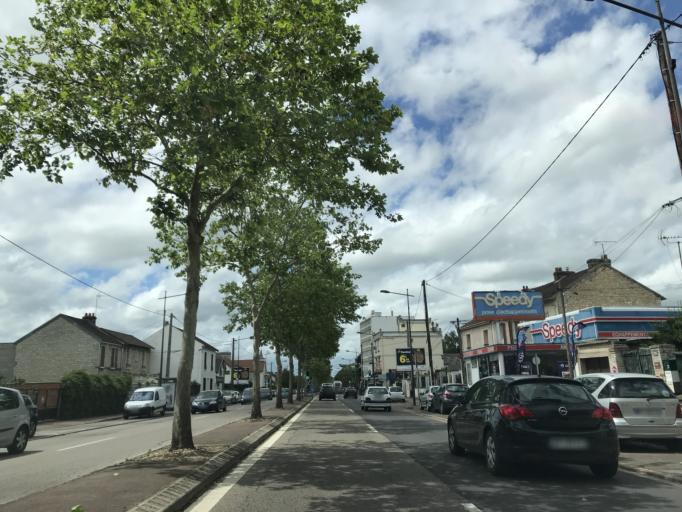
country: FR
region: Ile-de-France
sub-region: Departement des Yvelines
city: Mantes-la-Ville
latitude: 48.9941
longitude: 1.6969
